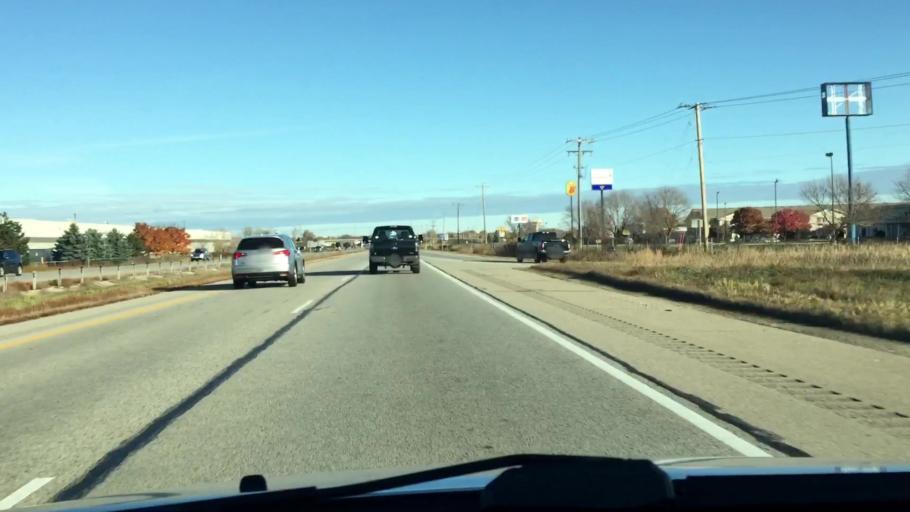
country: US
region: Wisconsin
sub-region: Fond du Lac County
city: North Fond du Lac
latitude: 43.7861
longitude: -88.4824
